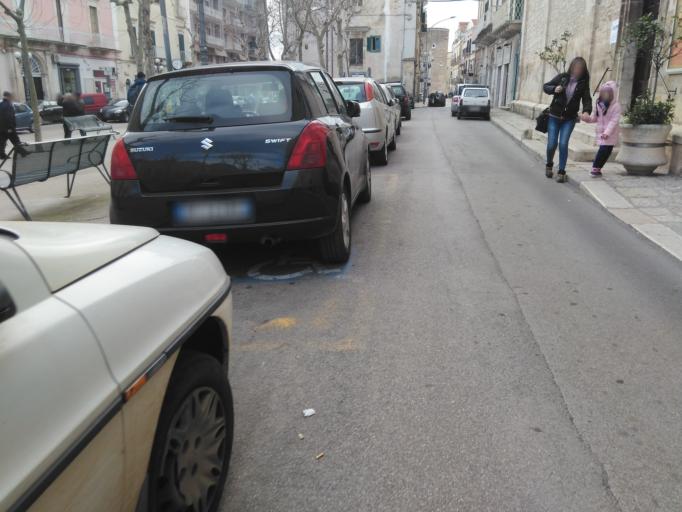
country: IT
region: Apulia
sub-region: Provincia di Bari
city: Bitonto
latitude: 41.1092
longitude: 16.6897
